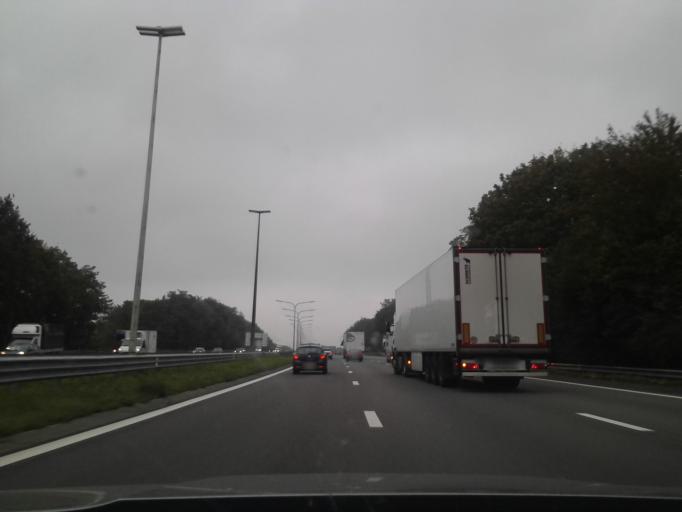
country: BE
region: Wallonia
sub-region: Province du Brabant Wallon
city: Nivelles
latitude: 50.5955
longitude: 4.2987
